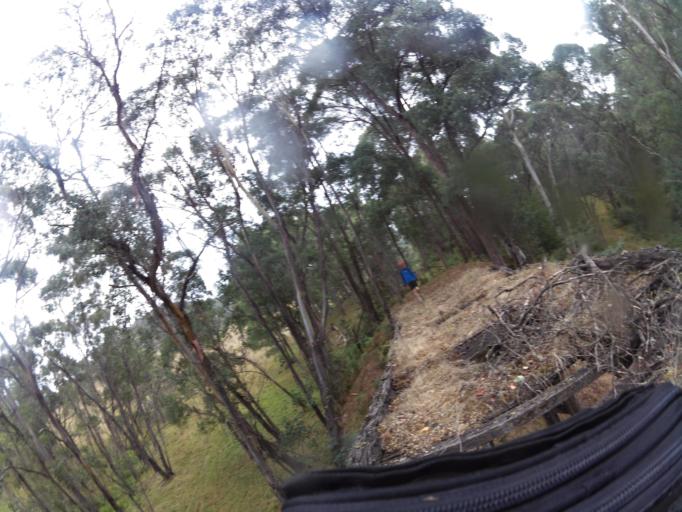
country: AU
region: New South Wales
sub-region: Greater Hume Shire
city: Holbrook
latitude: -36.2321
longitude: 147.6011
